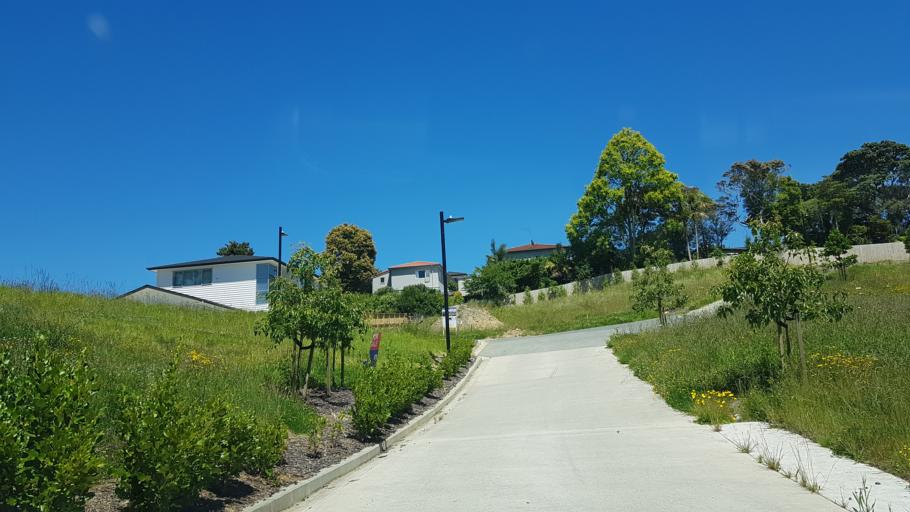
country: NZ
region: Auckland
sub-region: Auckland
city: North Shore
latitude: -36.8076
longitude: 174.7309
